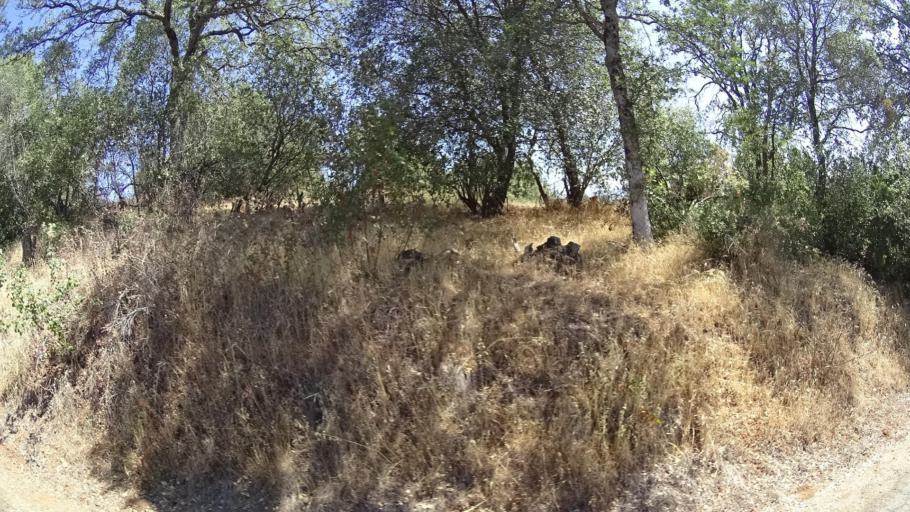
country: US
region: California
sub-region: Mariposa County
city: Mariposa
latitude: 37.4678
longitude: -119.9172
